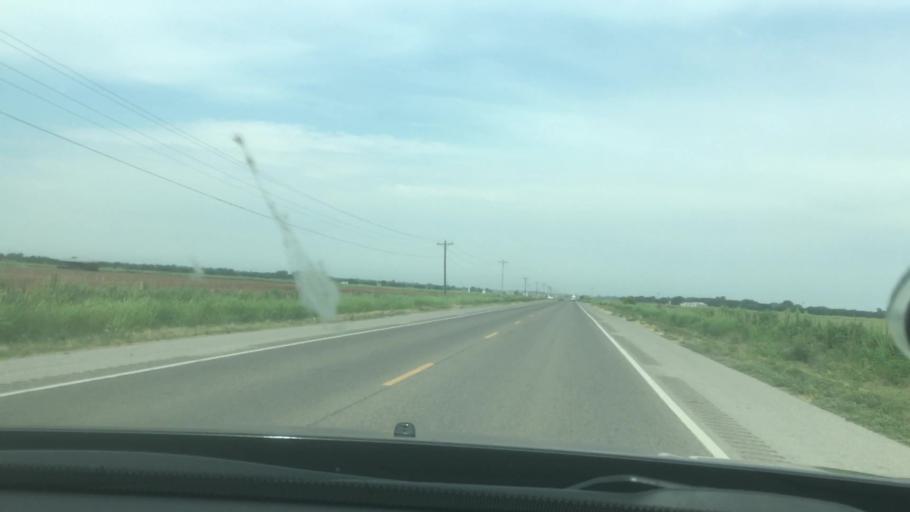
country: US
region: Oklahoma
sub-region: Garvin County
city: Maysville
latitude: 34.8216
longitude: -97.5034
